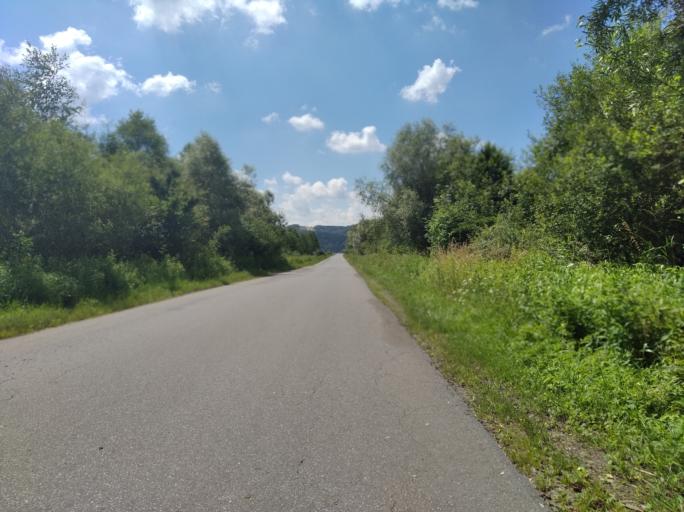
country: PL
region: Subcarpathian Voivodeship
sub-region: Powiat brzozowski
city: Dydnia
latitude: 49.7066
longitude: 22.2094
